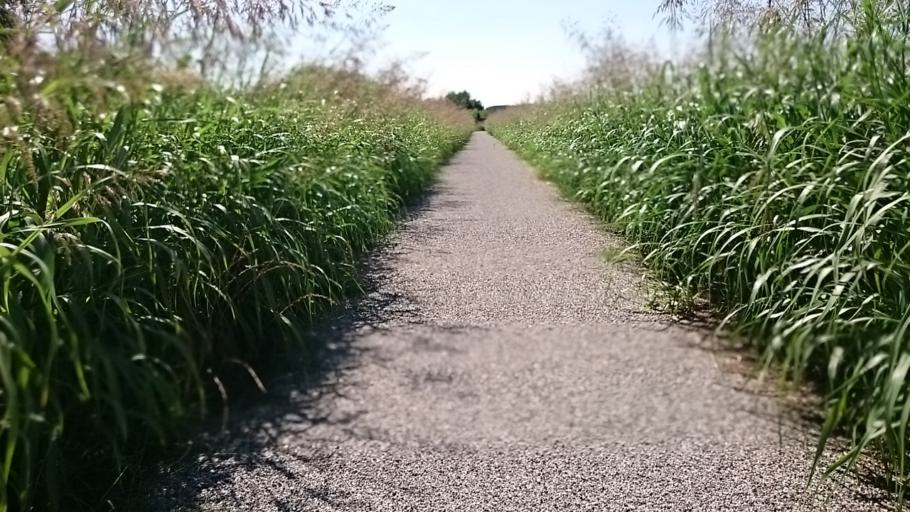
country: IT
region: Veneto
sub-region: Provincia di Padova
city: Cervarese Santa Croce
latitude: 45.4222
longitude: 11.7014
